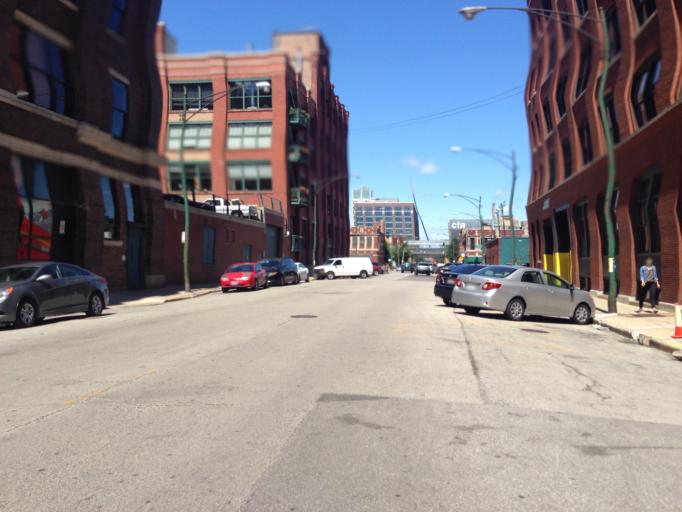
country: US
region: Illinois
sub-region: Cook County
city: Chicago
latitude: 41.8832
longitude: -87.6522
